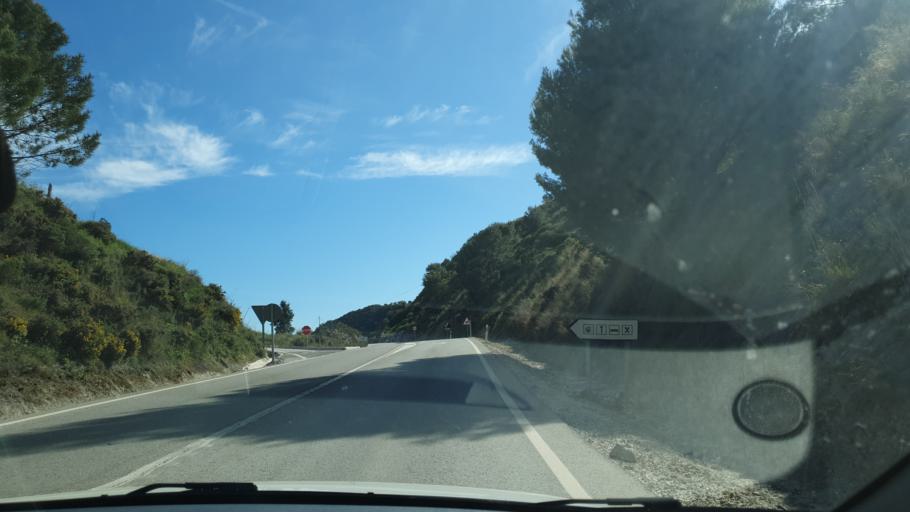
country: ES
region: Andalusia
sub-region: Provincia de Malaga
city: Ojen
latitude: 36.5835
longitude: -4.8527
